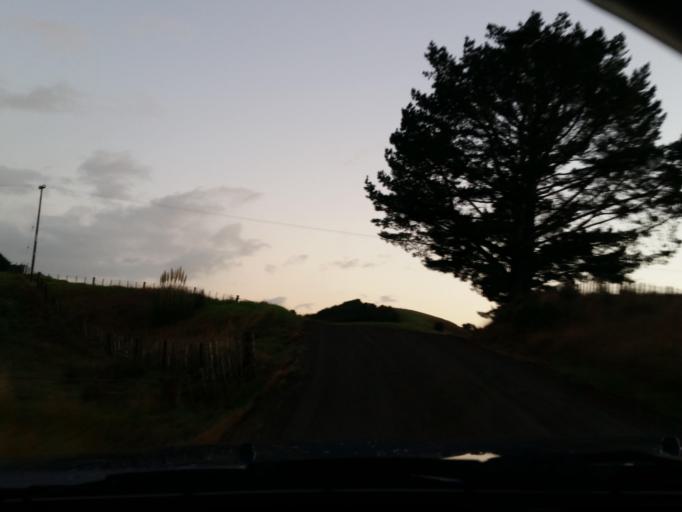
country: NZ
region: Northland
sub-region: Whangarei
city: Maungatapere
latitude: -35.8068
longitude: 174.0416
